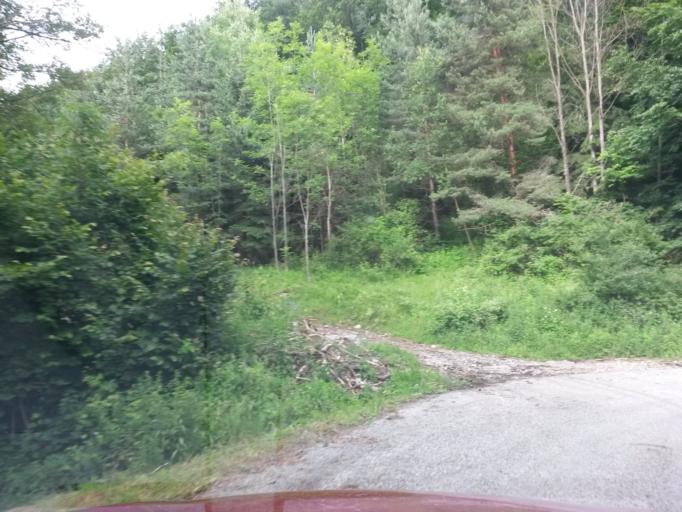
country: SK
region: Banskobystricky
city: Detva
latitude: 48.4591
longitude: 19.3126
